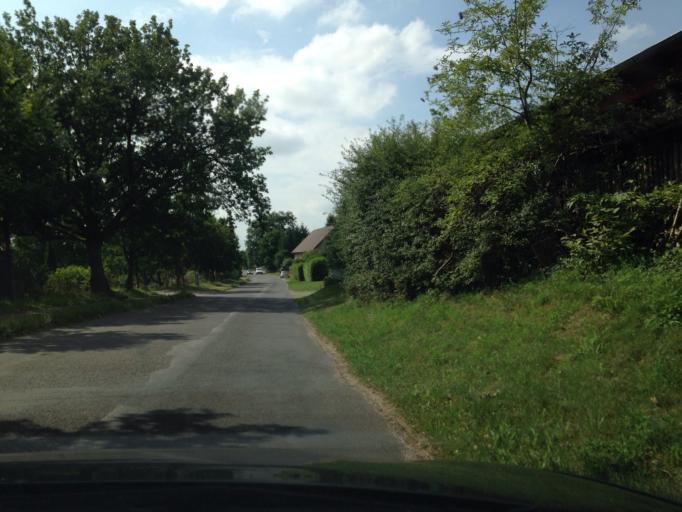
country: DE
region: Mecklenburg-Vorpommern
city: Loitz
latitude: 53.3242
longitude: 13.4151
